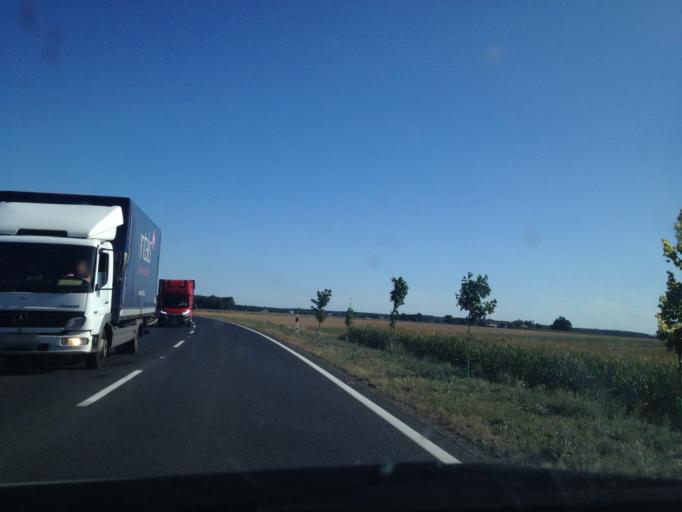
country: PL
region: Greater Poland Voivodeship
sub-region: Powiat poznanski
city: Kornik
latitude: 52.2431
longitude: 17.0540
